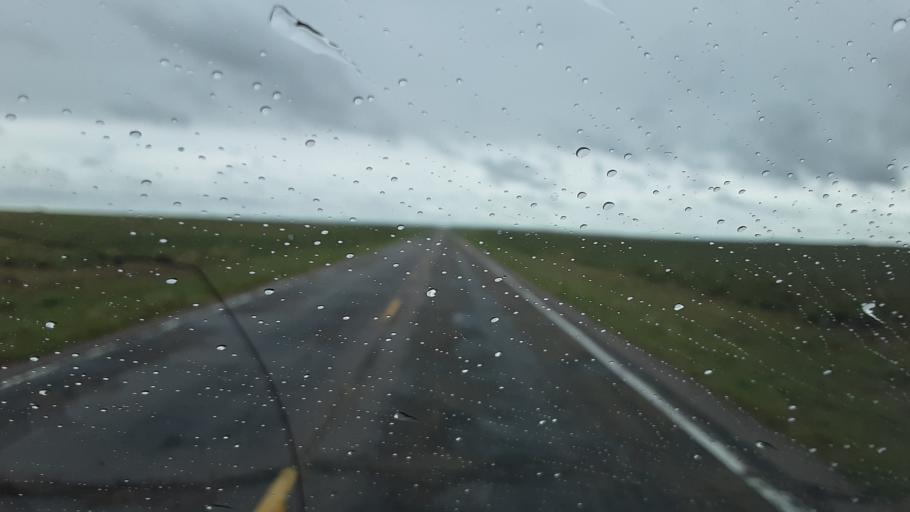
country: US
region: Colorado
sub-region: Lincoln County
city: Hugo
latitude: 38.8495
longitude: -103.2866
